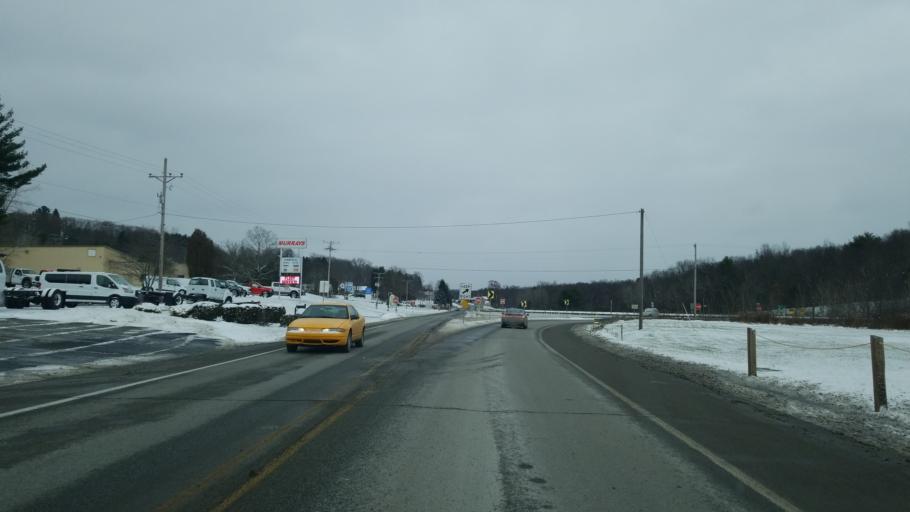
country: US
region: Pennsylvania
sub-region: Clearfield County
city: Sandy
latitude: 41.0916
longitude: -78.7728
